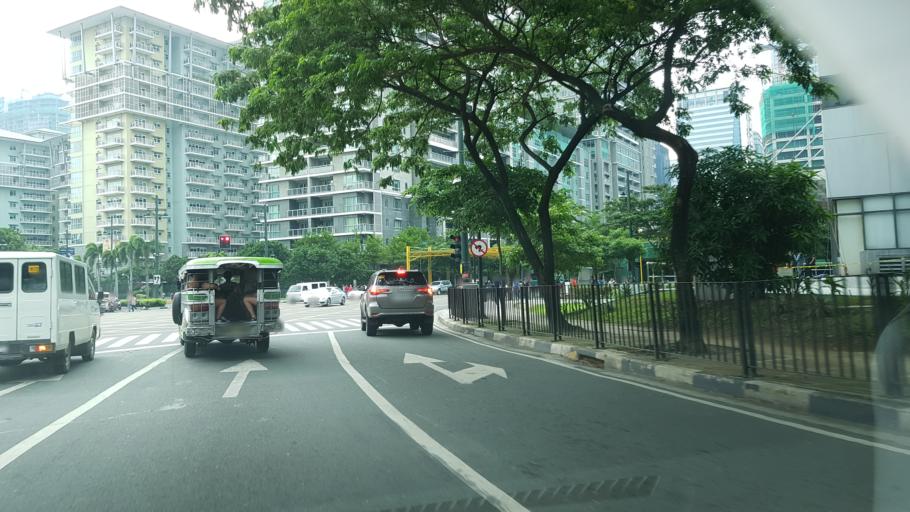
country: PH
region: Calabarzon
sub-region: Province of Rizal
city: Pateros
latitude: 14.5521
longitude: 121.0565
